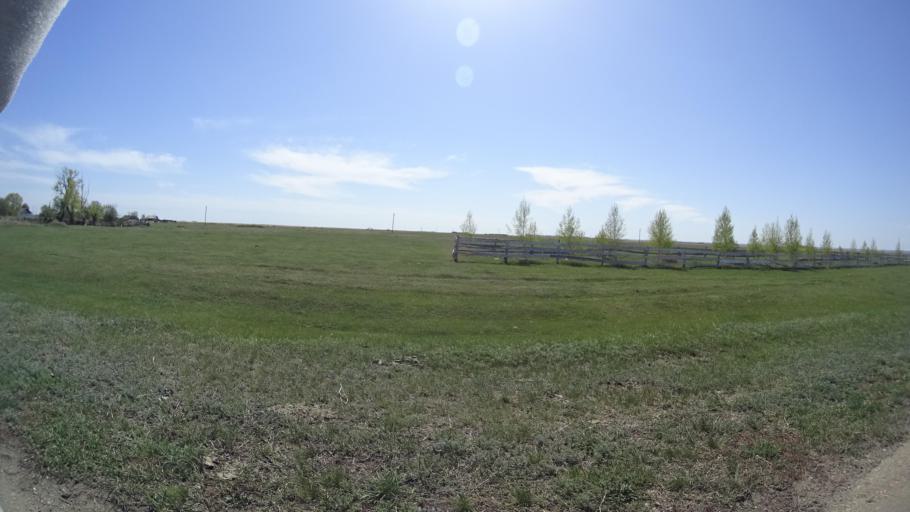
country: RU
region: Chelyabinsk
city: Chesma
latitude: 53.8020
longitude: 61.0158
